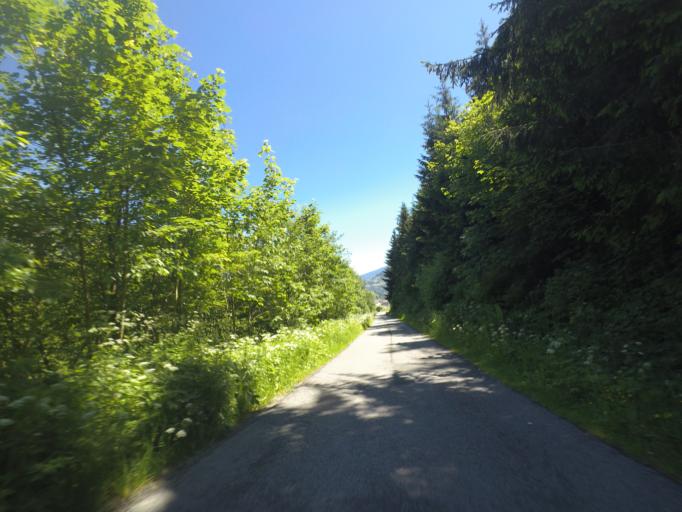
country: AT
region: Salzburg
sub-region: Politischer Bezirk Sankt Johann im Pongau
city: Goldegg
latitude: 47.3242
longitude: 13.1237
